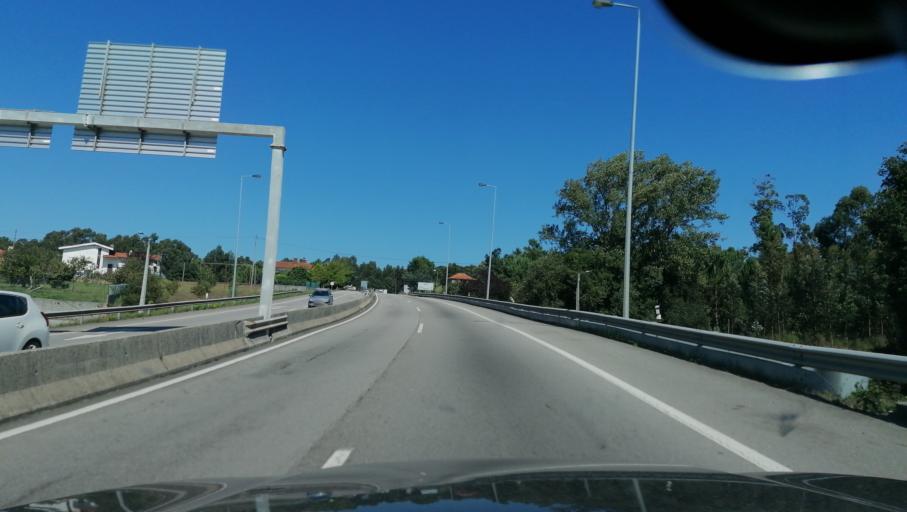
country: PT
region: Aveiro
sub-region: Santa Maria da Feira
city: Feira
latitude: 40.9238
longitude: -8.5764
